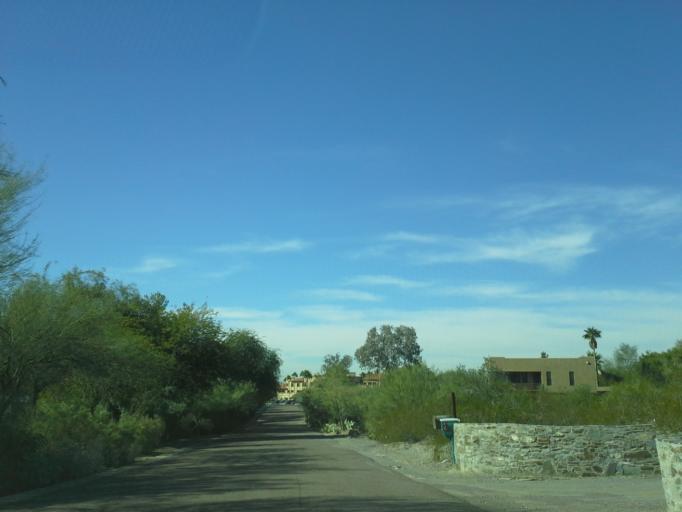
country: US
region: Arizona
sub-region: Maricopa County
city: Paradise Valley
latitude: 33.5524
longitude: -112.0452
